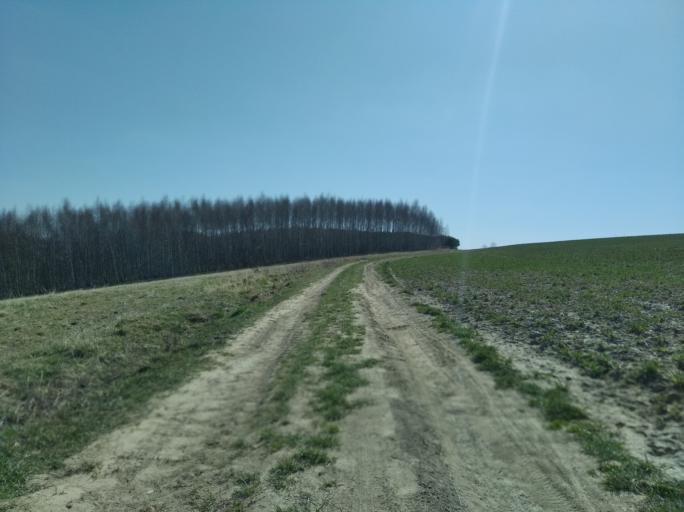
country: PL
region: Subcarpathian Voivodeship
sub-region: Powiat strzyzowski
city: Polomia
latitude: 49.8821
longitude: 21.8556
